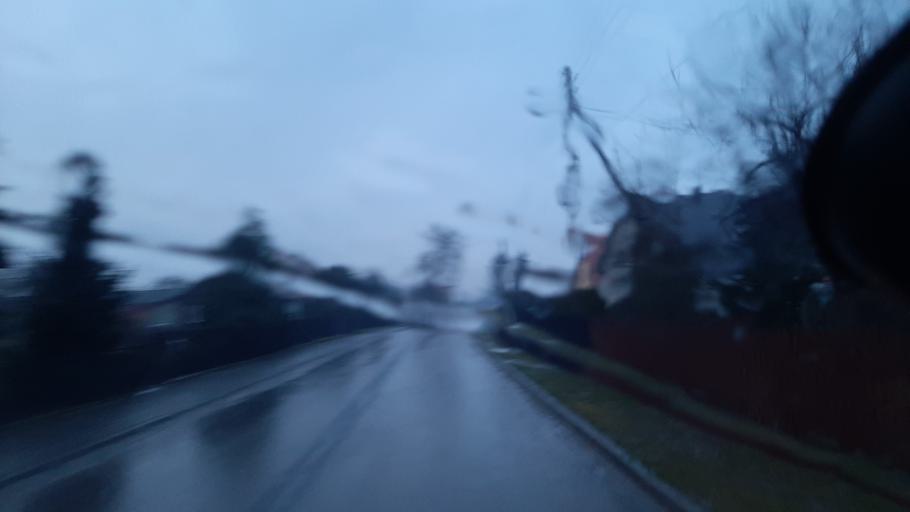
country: PL
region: Lublin Voivodeship
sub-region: Powiat lubartowski
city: Firlej
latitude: 51.5450
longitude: 22.5635
